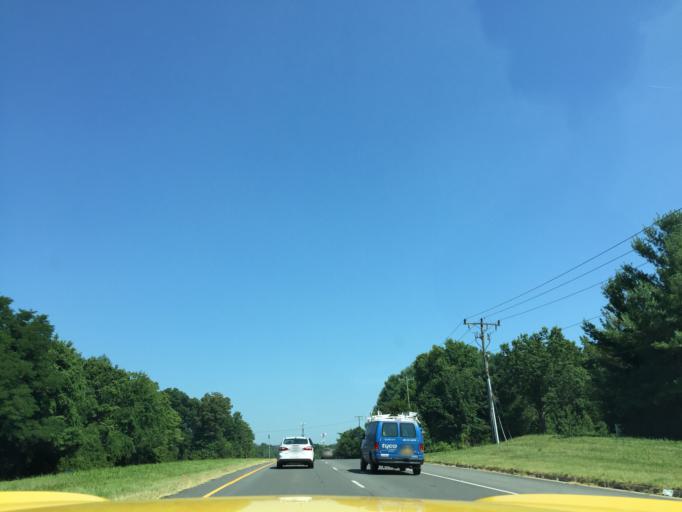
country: US
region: Virginia
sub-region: Fairfax County
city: Reston
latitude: 38.9818
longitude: -77.3204
